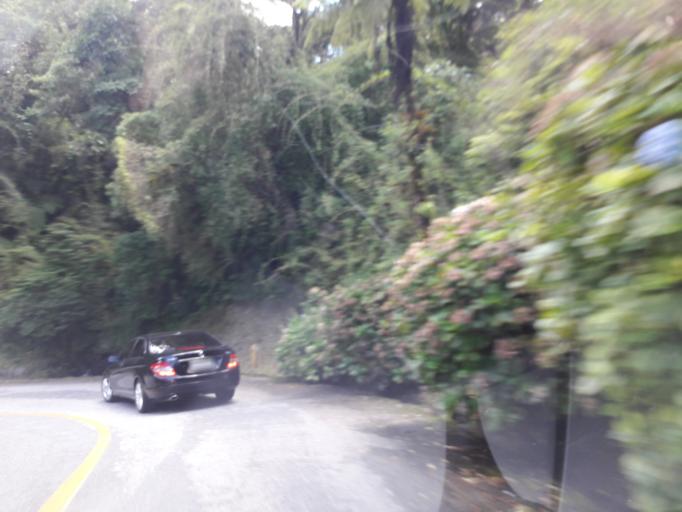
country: BR
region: Parana
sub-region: Campina Grande Do Sul
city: Campina Grande do Sul
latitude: -25.3309
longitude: -48.8979
